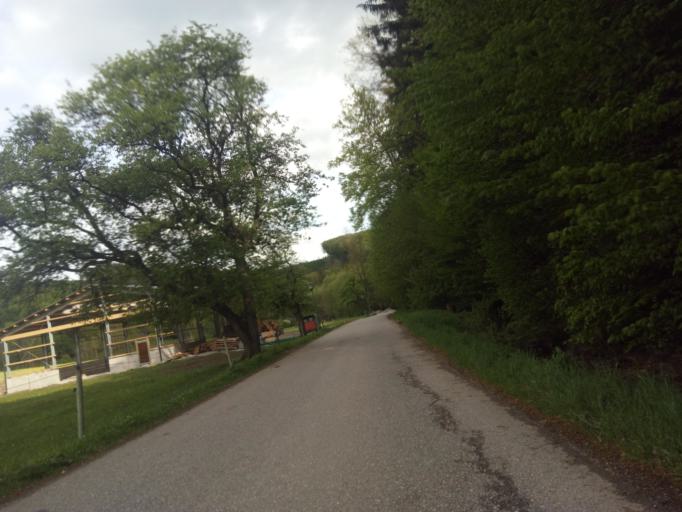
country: AT
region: Lower Austria
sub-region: Politischer Bezirk Wien-Umgebung
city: Wolfsgraben
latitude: 48.1251
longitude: 16.0928
